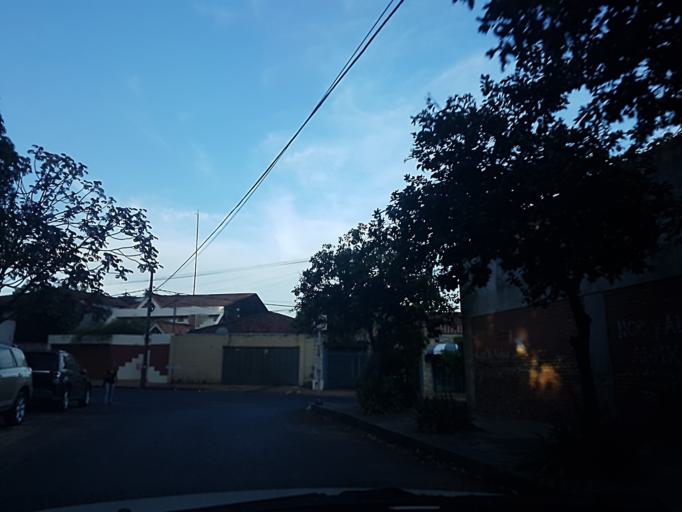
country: PY
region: Asuncion
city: Asuncion
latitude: -25.2845
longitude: -57.5921
